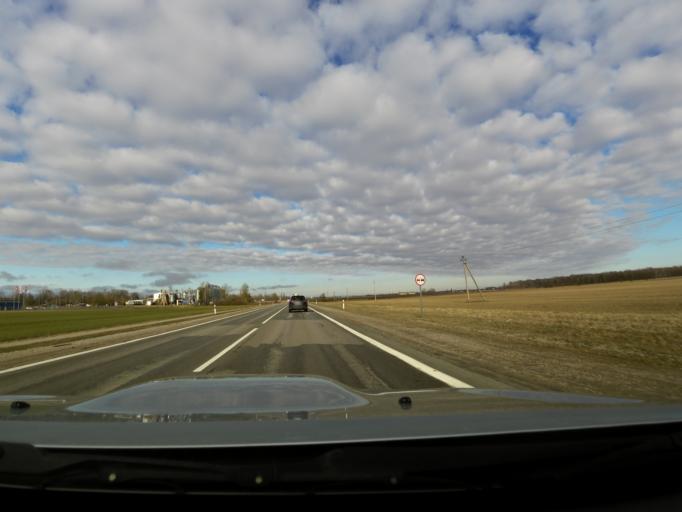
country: LT
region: Panevezys
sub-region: Panevezys City
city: Panevezys
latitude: 55.7472
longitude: 24.1590
